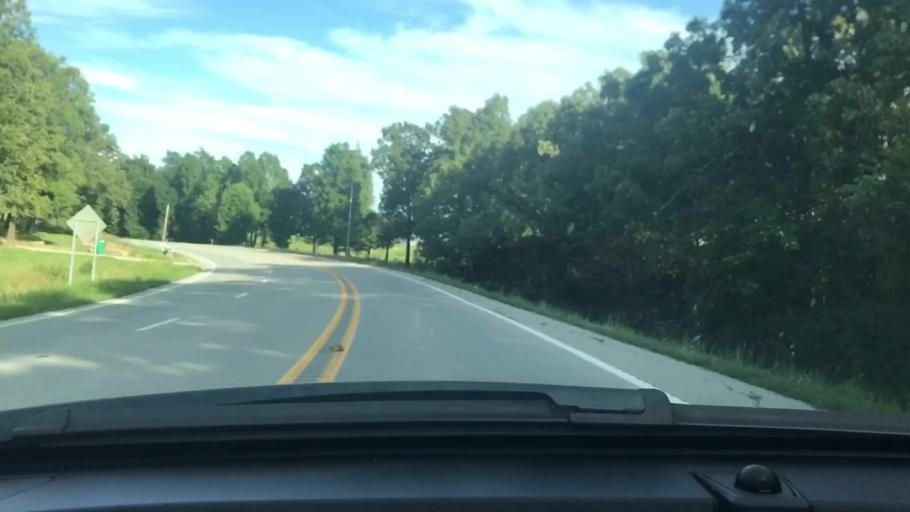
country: US
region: Arkansas
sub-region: Sharp County
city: Cherokee Village
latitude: 36.2719
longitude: -91.3704
